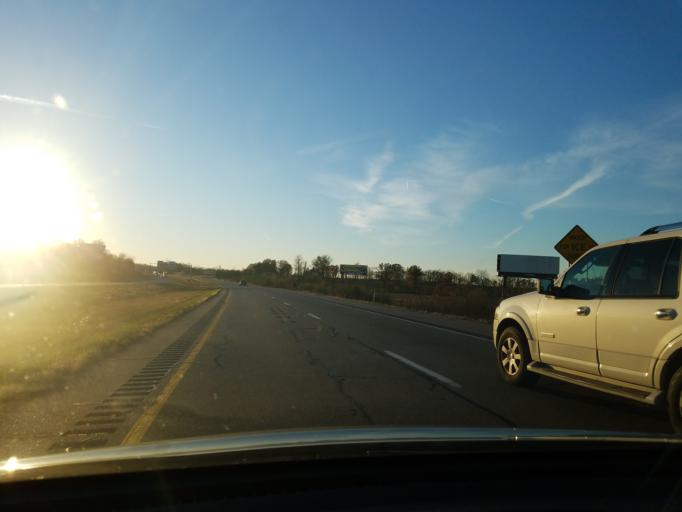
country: US
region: Indiana
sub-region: Gibson County
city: Haubstadt
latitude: 38.1696
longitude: -87.4905
